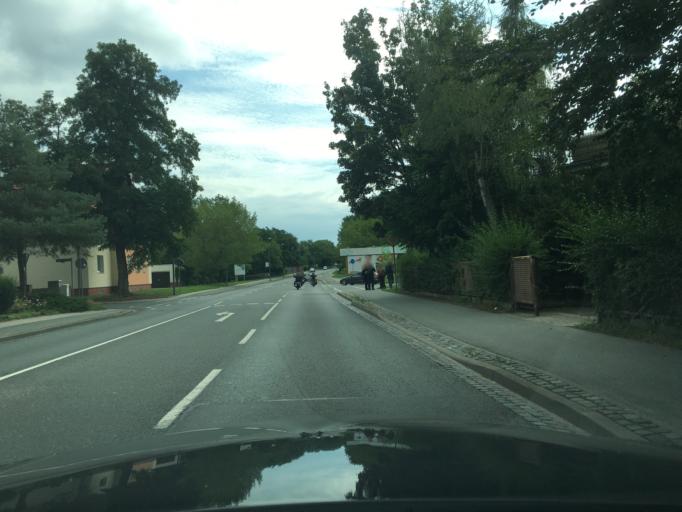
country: DE
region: Saxony-Anhalt
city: Holzweissig
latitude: 51.6138
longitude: 12.2961
